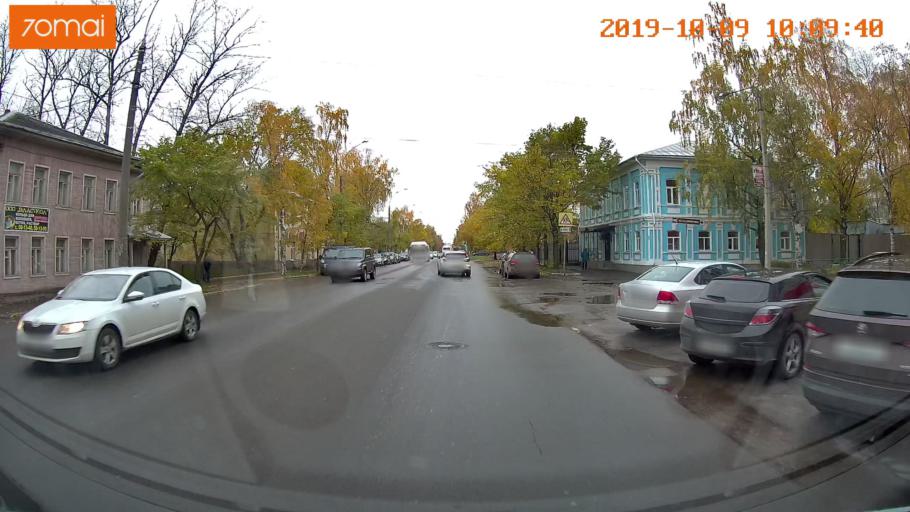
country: RU
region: Vologda
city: Vologda
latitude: 59.2130
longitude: 39.9022
